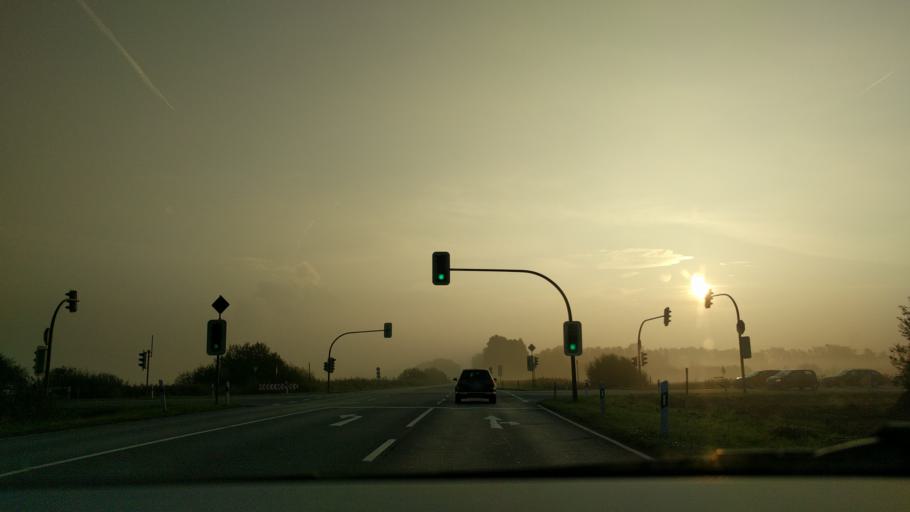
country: DE
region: Lower Saxony
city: Weyhausen
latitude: 52.4354
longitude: 10.7140
